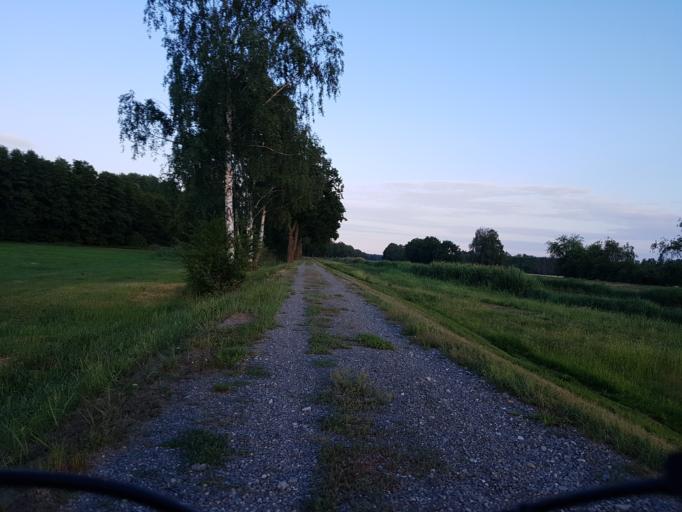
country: DE
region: Brandenburg
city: Schilda
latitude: 51.5845
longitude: 13.3360
